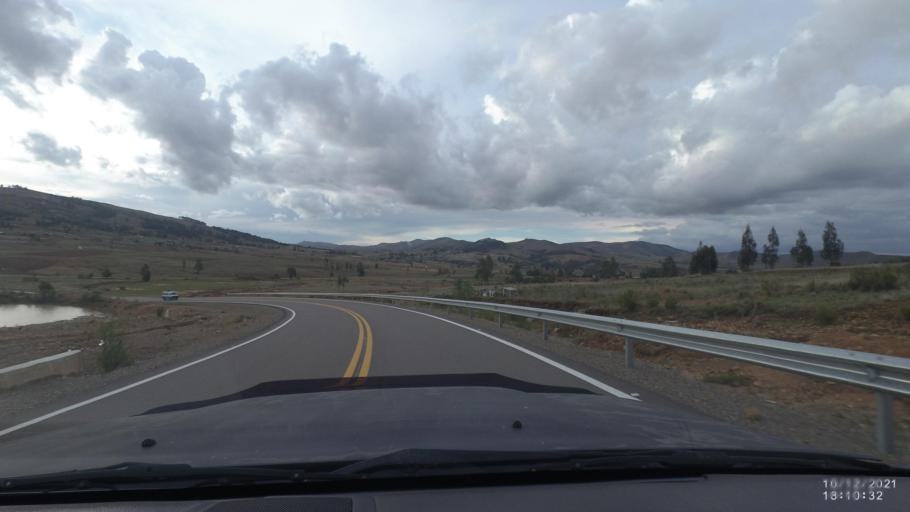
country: BO
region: Cochabamba
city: Tarata
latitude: -17.7845
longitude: -65.9580
